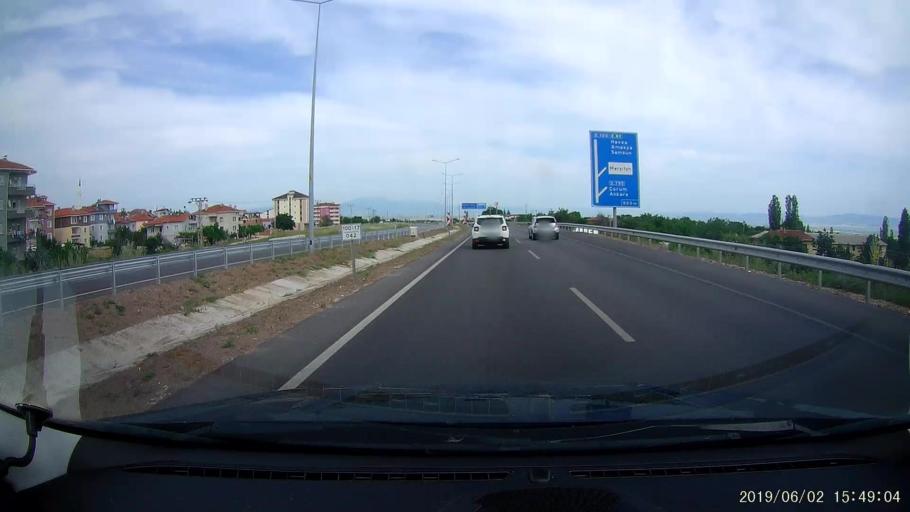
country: TR
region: Amasya
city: Merzifon
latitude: 40.8590
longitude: 35.4545
